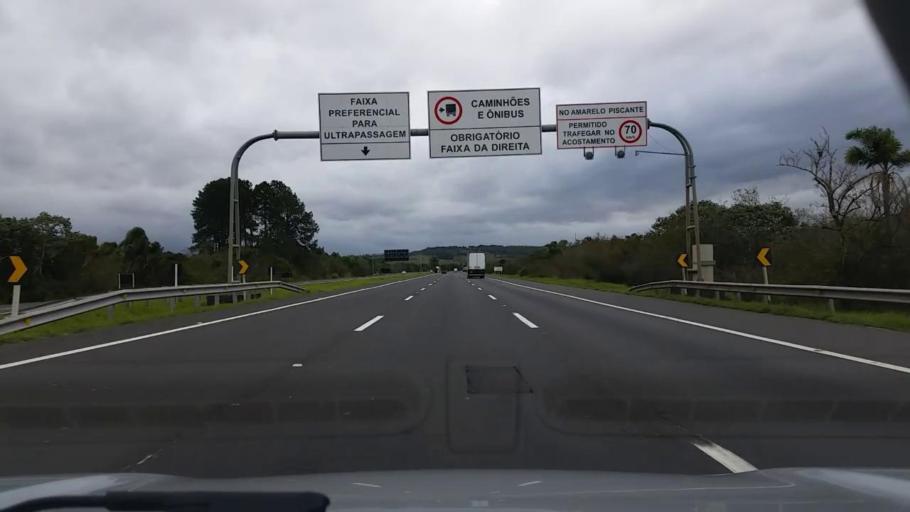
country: BR
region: Rio Grande do Sul
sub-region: Osorio
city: Osorio
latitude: -29.8874
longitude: -50.4545
